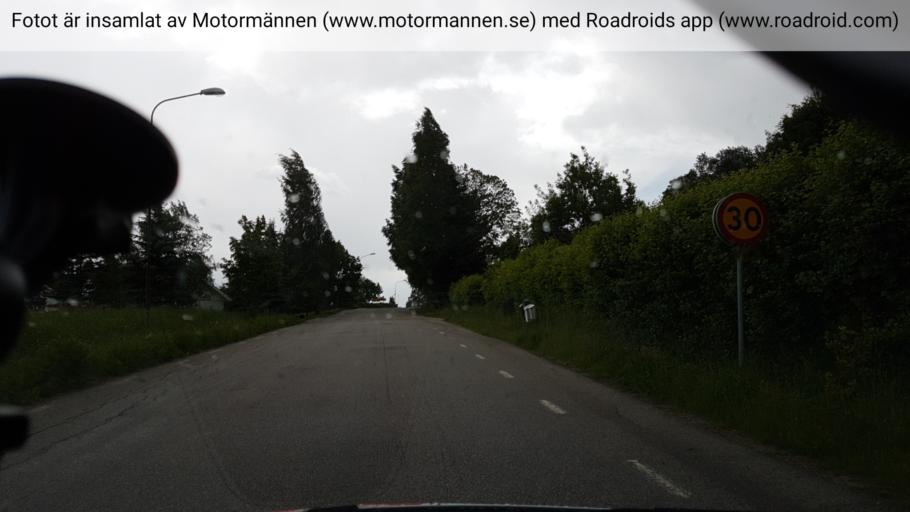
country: SE
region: Gaevleborg
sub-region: Bollnas Kommun
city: Kilafors
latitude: 61.2596
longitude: 16.7941
